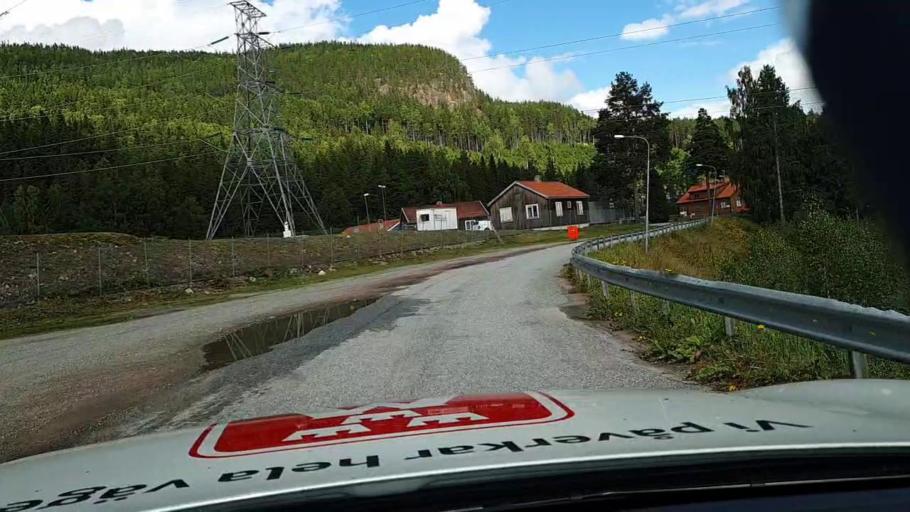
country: SE
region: Jaemtland
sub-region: Ragunda Kommun
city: Hammarstrand
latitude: 63.1468
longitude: 16.0745
